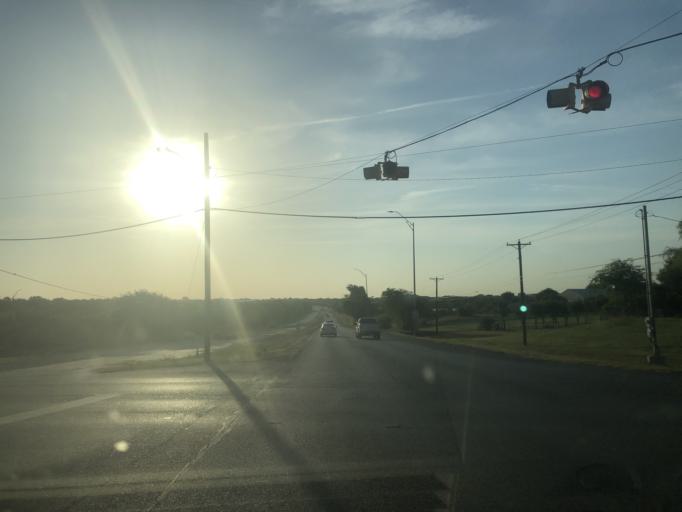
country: US
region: Texas
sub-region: Tarrant County
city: White Settlement
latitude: 32.7205
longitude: -97.5192
